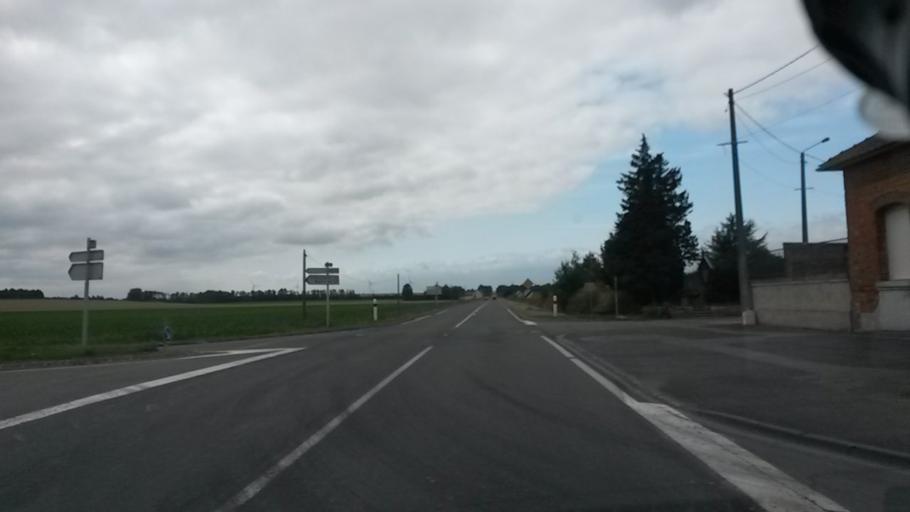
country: FR
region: Nord-Pas-de-Calais
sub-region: Departement du Pas-de-Calais
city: Bourlon
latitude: 50.1593
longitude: 3.1244
